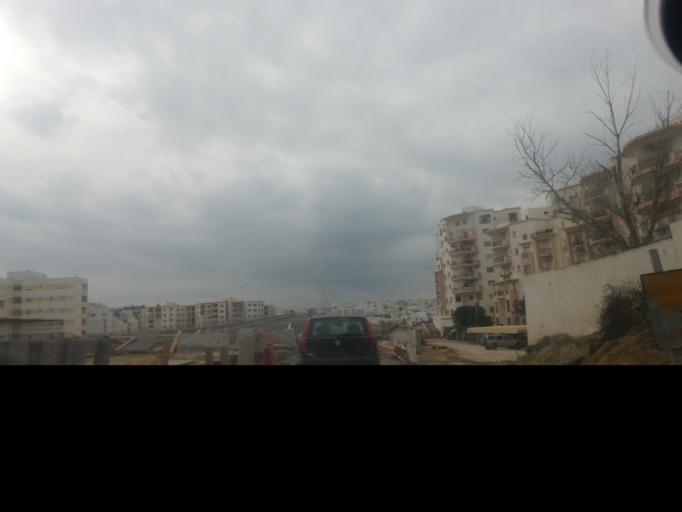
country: TN
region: Tunis
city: Tunis
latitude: 36.8551
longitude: 10.1555
